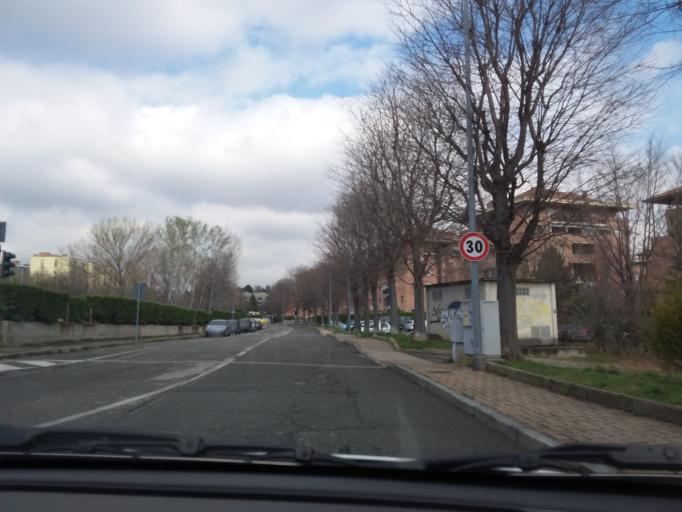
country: IT
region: Piedmont
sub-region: Provincia di Torino
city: Rivoli
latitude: 45.0630
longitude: 7.5278
